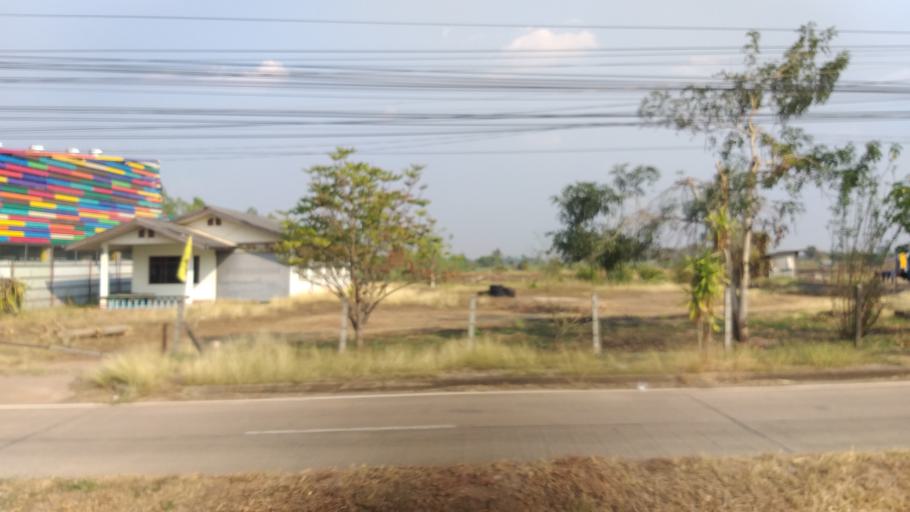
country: TH
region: Changwat Udon Thani
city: Non Sa-at
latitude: 16.9603
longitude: 102.8926
